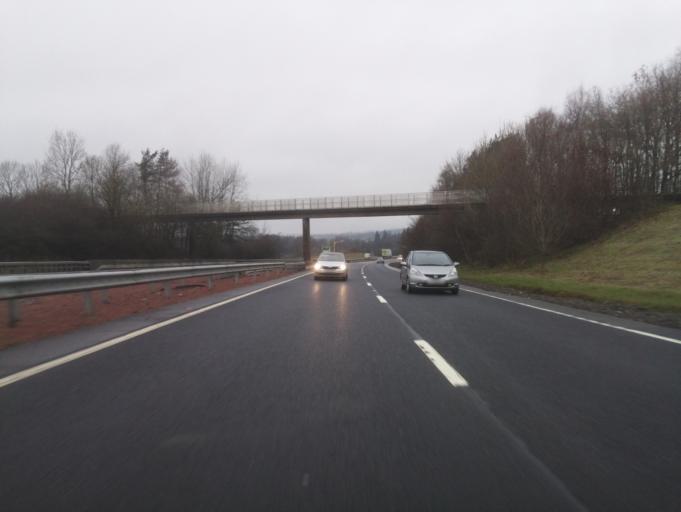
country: GB
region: Scotland
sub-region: Stirling
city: Dunblane
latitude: 56.1834
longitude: -3.9839
